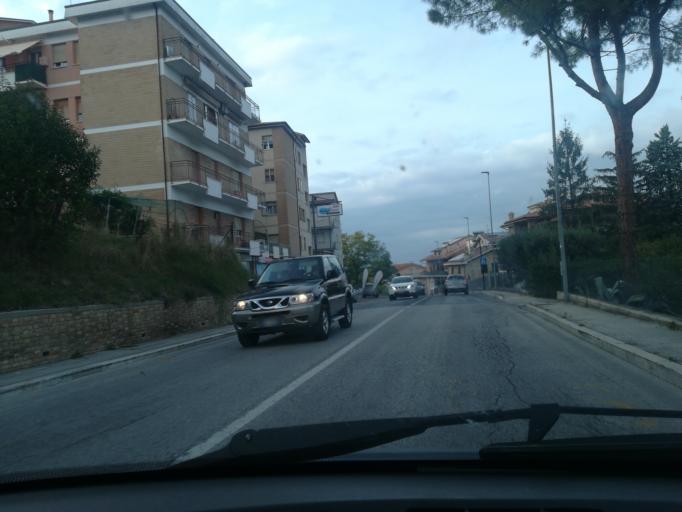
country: IT
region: The Marches
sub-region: Provincia di Macerata
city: Villa Potenza
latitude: 43.3079
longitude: 13.4378
